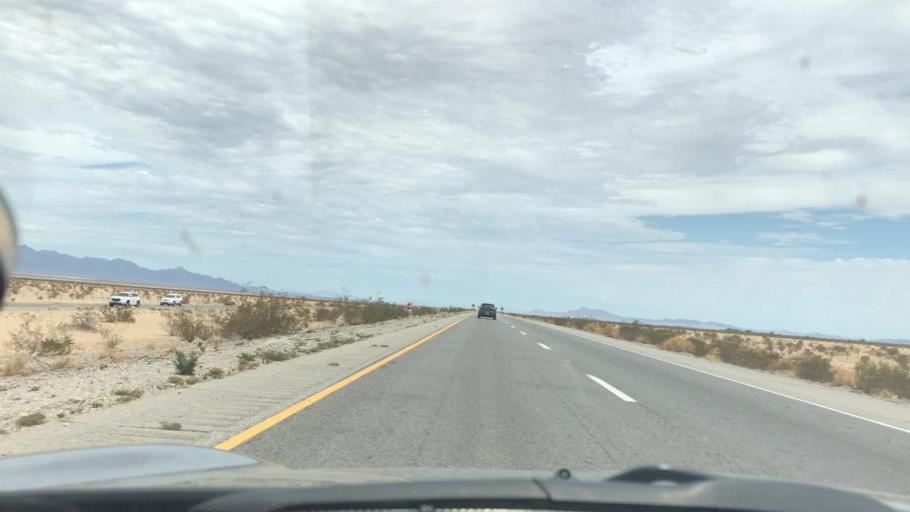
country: US
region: California
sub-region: Riverside County
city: Mesa Verde
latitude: 33.6395
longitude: -115.0967
